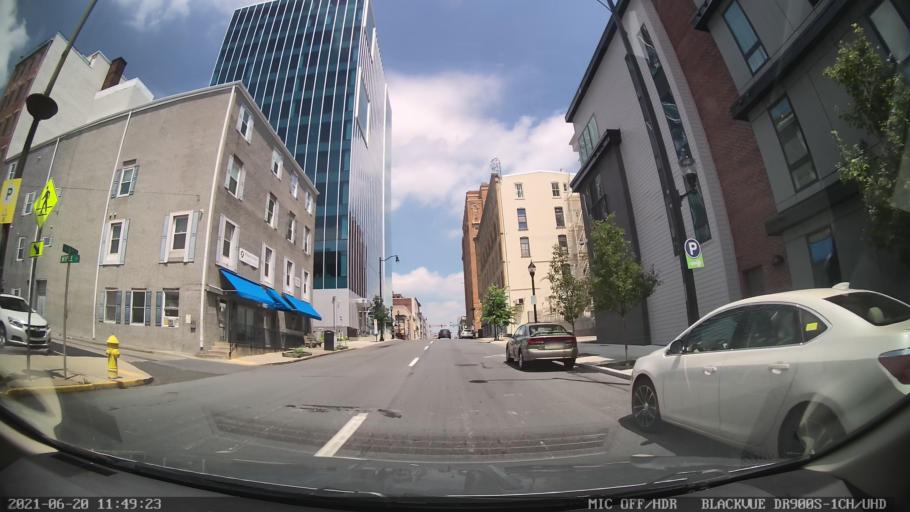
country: US
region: Pennsylvania
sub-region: Lehigh County
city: Allentown
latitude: 40.6018
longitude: -75.4694
